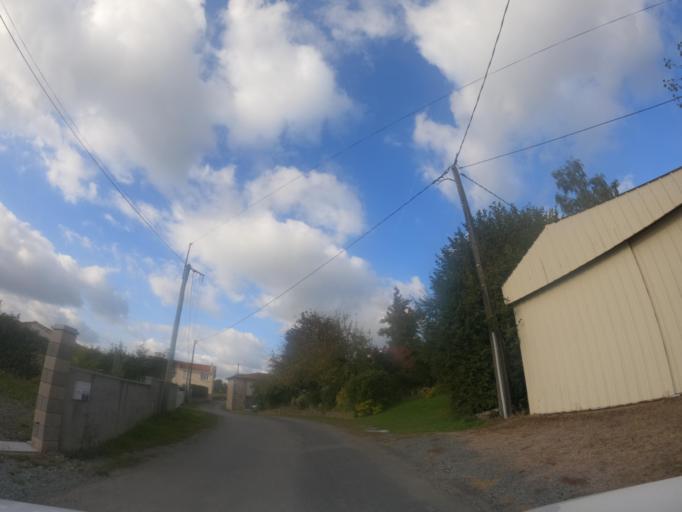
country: FR
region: Poitou-Charentes
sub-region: Departement des Deux-Sevres
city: Courlay
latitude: 46.7931
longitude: -0.6070
